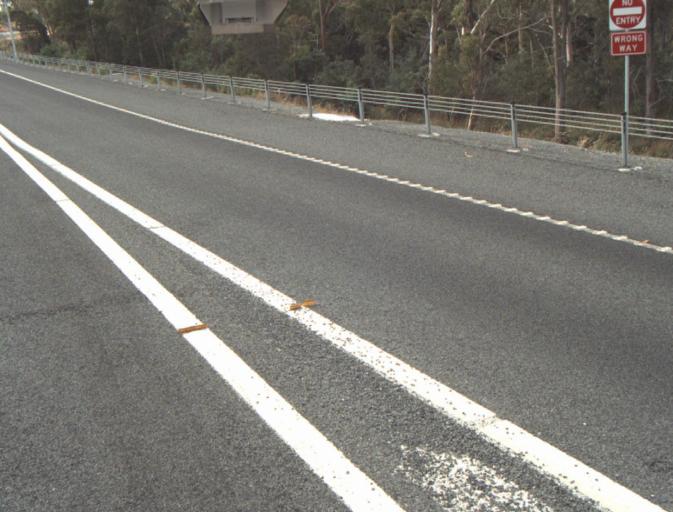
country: AU
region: Tasmania
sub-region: Launceston
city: Mayfield
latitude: -41.3019
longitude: 147.0506
